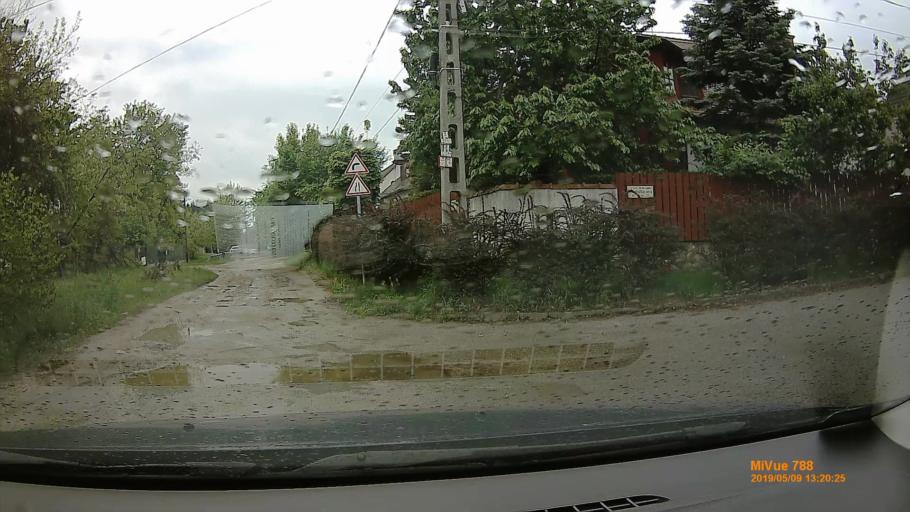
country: HU
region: Budapest
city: Budapest XVI. keruelet
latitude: 47.5400
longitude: 19.1886
